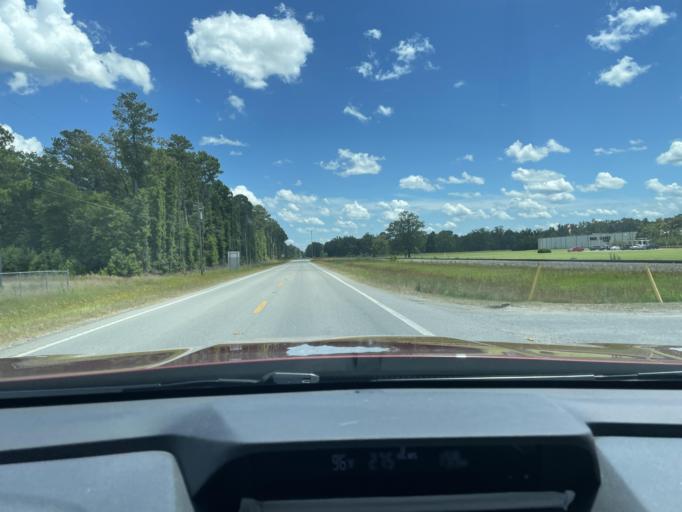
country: US
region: Arkansas
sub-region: Drew County
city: Monticello
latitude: 33.6171
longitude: -91.7457
